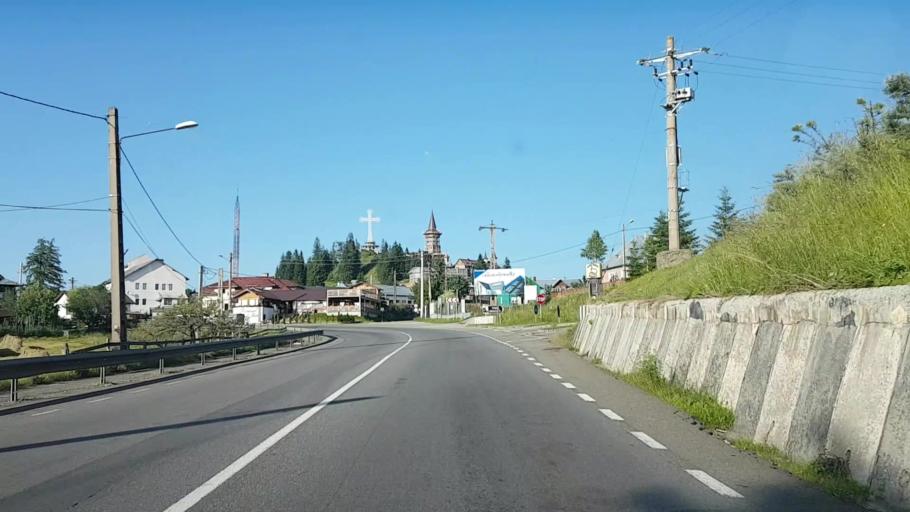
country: RO
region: Bistrita-Nasaud
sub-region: Comuna Lunca Ilvei
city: Lunca Ilvei
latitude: 47.2369
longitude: 25.0041
